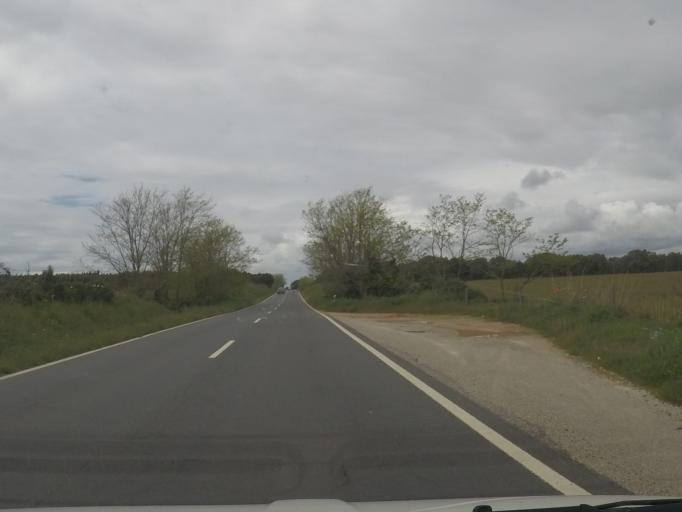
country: PT
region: Setubal
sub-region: Santiago do Cacem
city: Cercal
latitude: 37.8440
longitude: -8.7059
